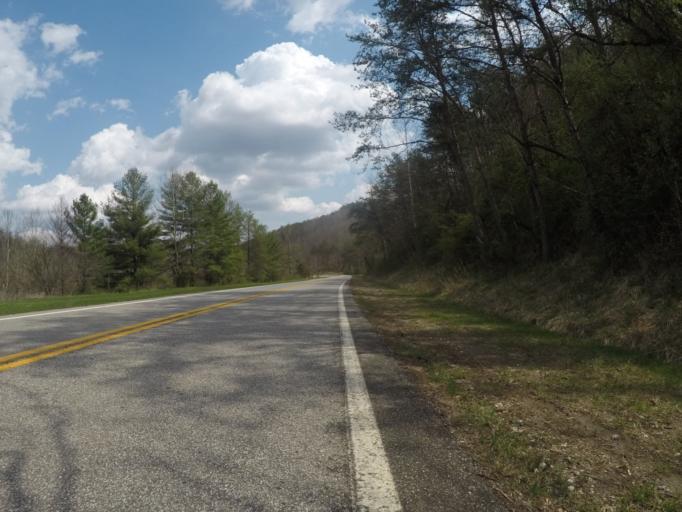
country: US
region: West Virginia
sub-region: Wayne County
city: Lavalette
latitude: 38.3084
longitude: -82.3436
